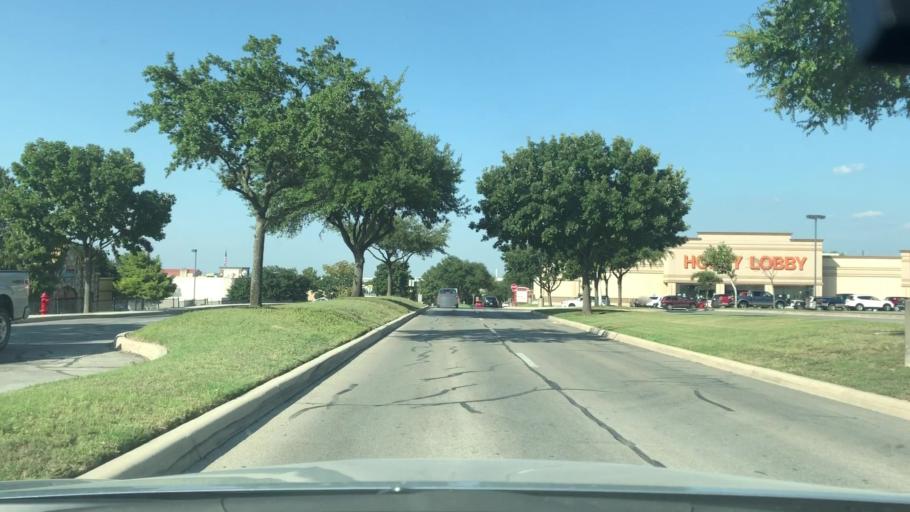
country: US
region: Texas
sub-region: Bexar County
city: Live Oak
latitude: 29.5744
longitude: -98.3236
